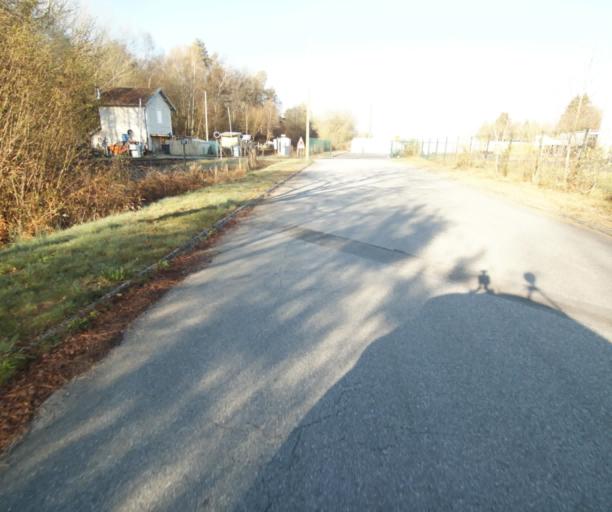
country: FR
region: Limousin
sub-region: Departement de la Correze
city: Correze
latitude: 45.3310
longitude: 1.8896
